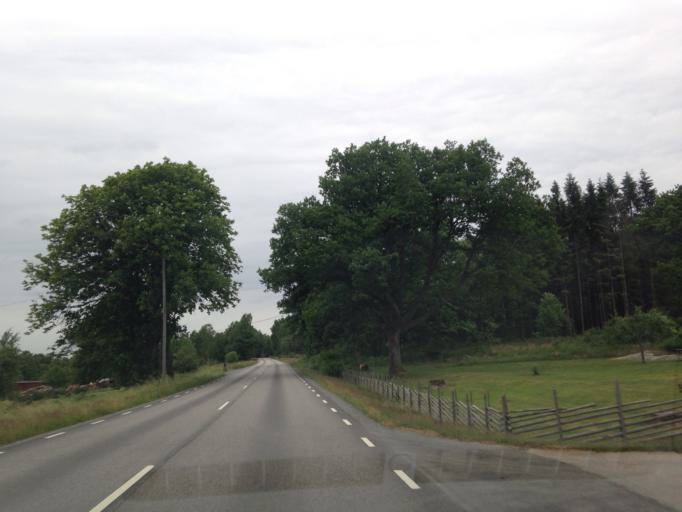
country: SE
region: Vaestra Goetaland
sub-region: Marks Kommun
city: Bua
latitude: 57.5120
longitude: 12.5501
